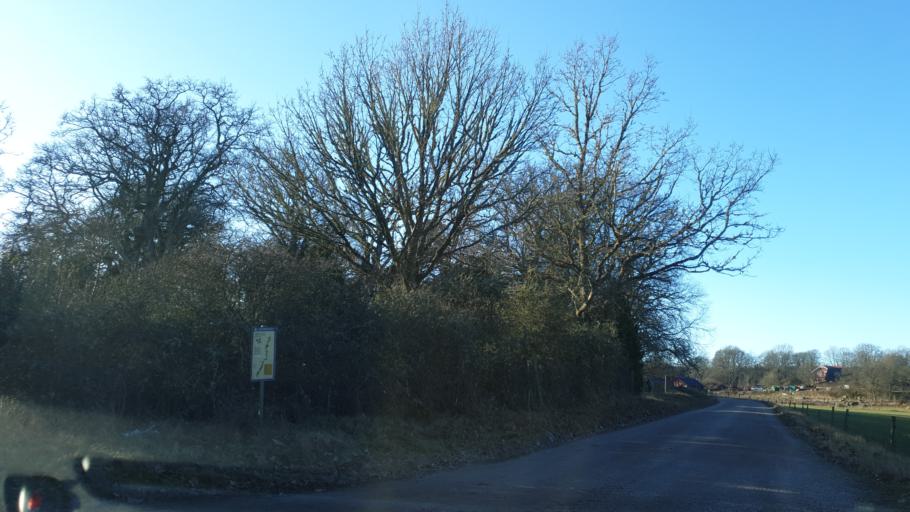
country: SE
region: Blekinge
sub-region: Karlskrona Kommun
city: Nattraby
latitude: 56.2608
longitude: 15.4268
